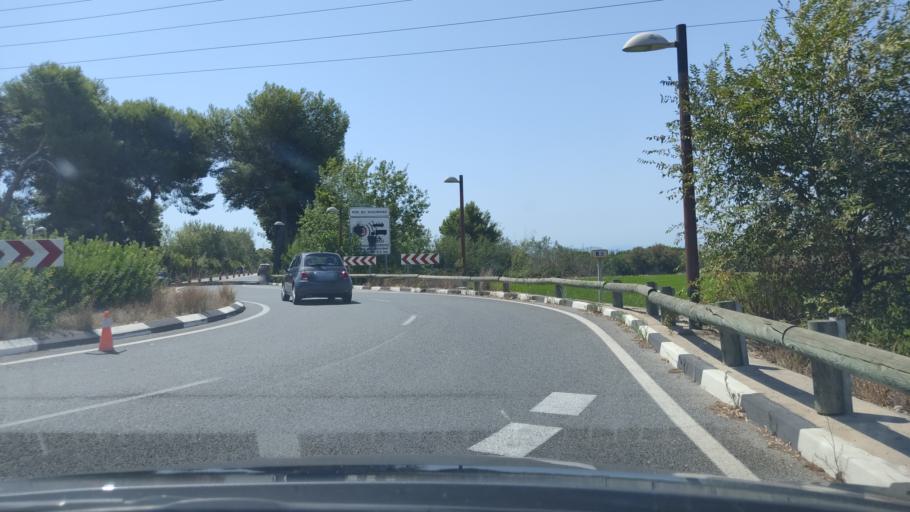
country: ES
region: Valencia
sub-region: Provincia de Valencia
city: Alfafar
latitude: 39.3591
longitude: -0.3266
